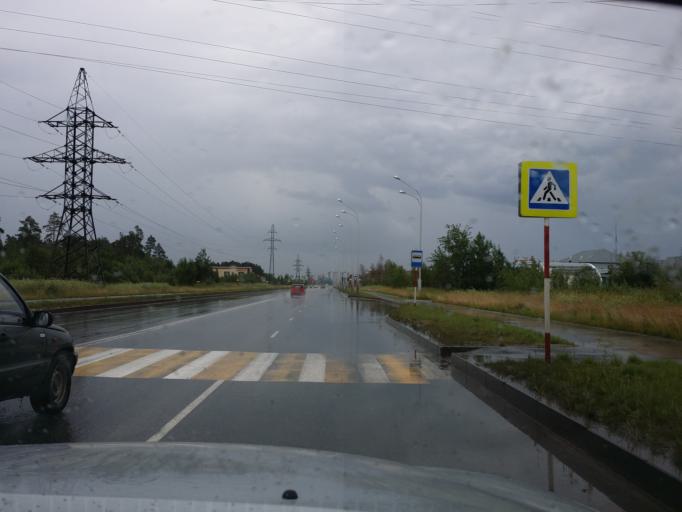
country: RU
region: Khanty-Mansiyskiy Avtonomnyy Okrug
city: Nizhnevartovsk
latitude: 60.9652
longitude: 76.5459
